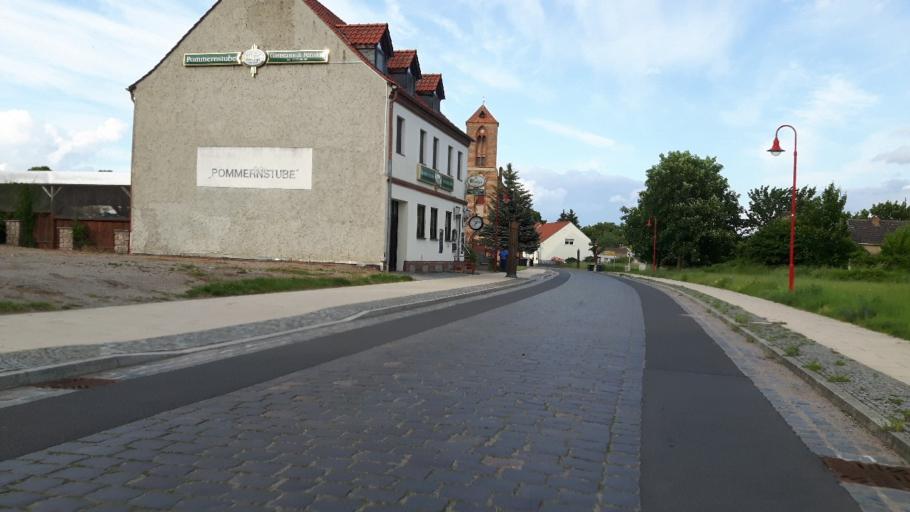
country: DE
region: Brandenburg
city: Gartz
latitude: 53.2081
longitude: 14.3930
